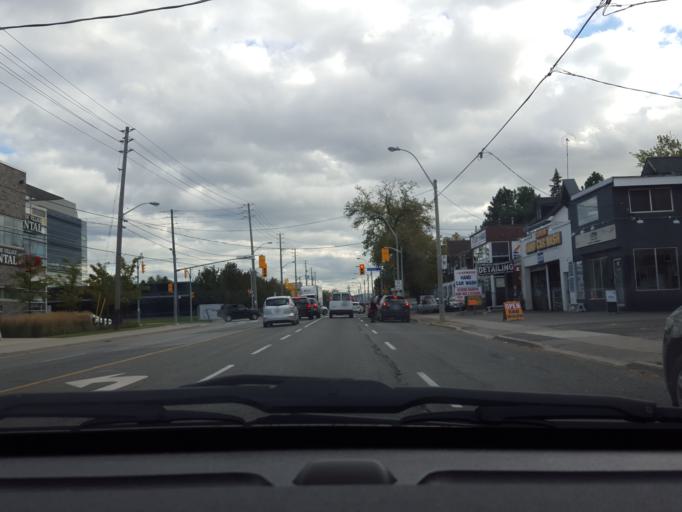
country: CA
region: Ontario
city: Toronto
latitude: 43.7059
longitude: -79.3617
